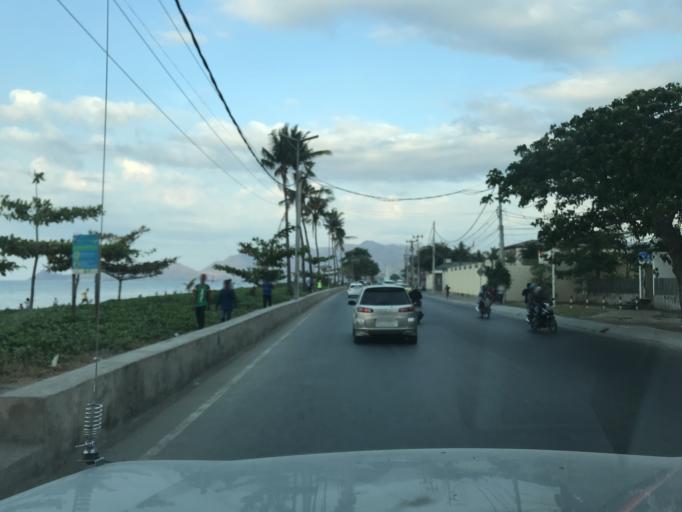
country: TL
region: Dili
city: Dili
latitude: -8.5482
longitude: 125.5621
